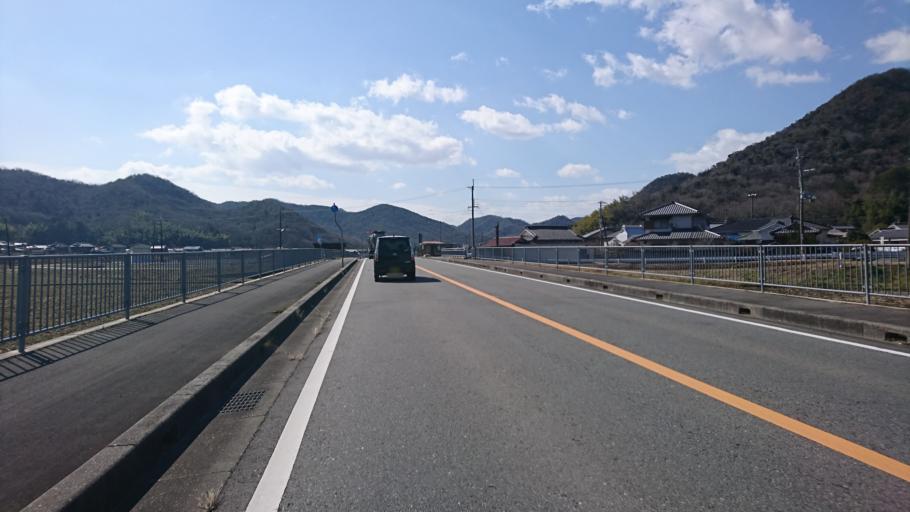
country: JP
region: Hyogo
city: Kakogawacho-honmachi
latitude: 34.8628
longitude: 134.7912
